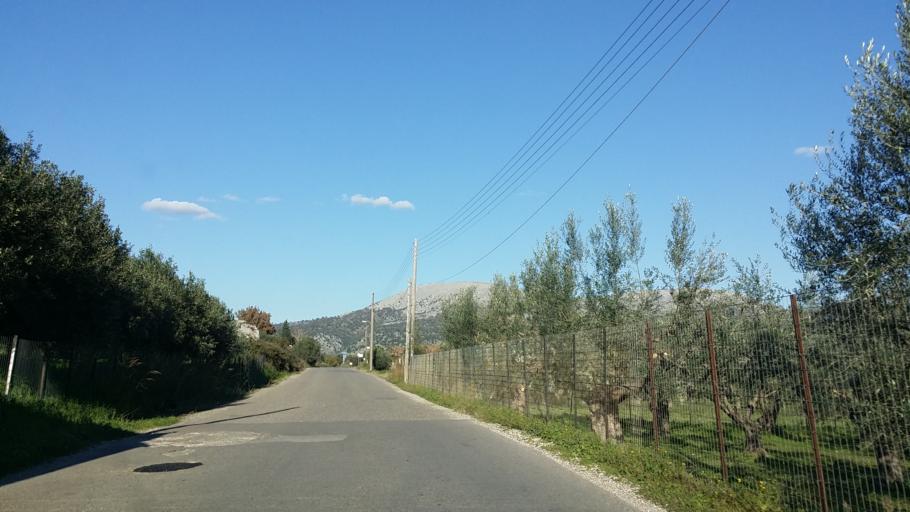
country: GR
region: West Greece
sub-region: Nomos Aitolias kai Akarnanias
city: Astakos
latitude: 38.5455
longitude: 21.0923
